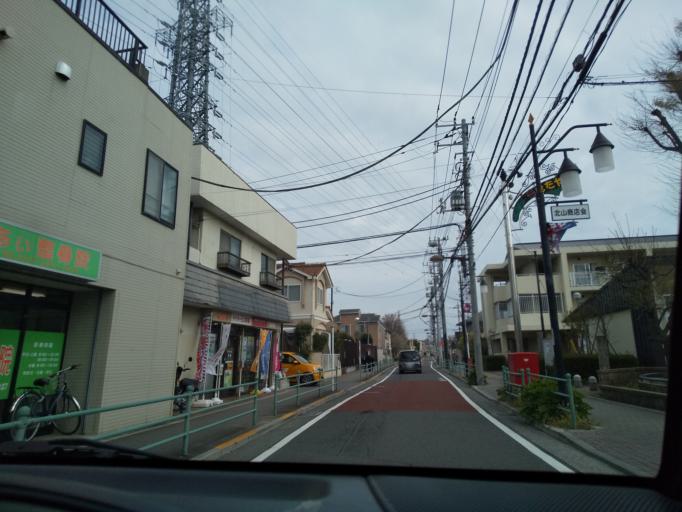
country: JP
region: Tokyo
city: Kokubunji
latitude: 35.6891
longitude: 139.4556
